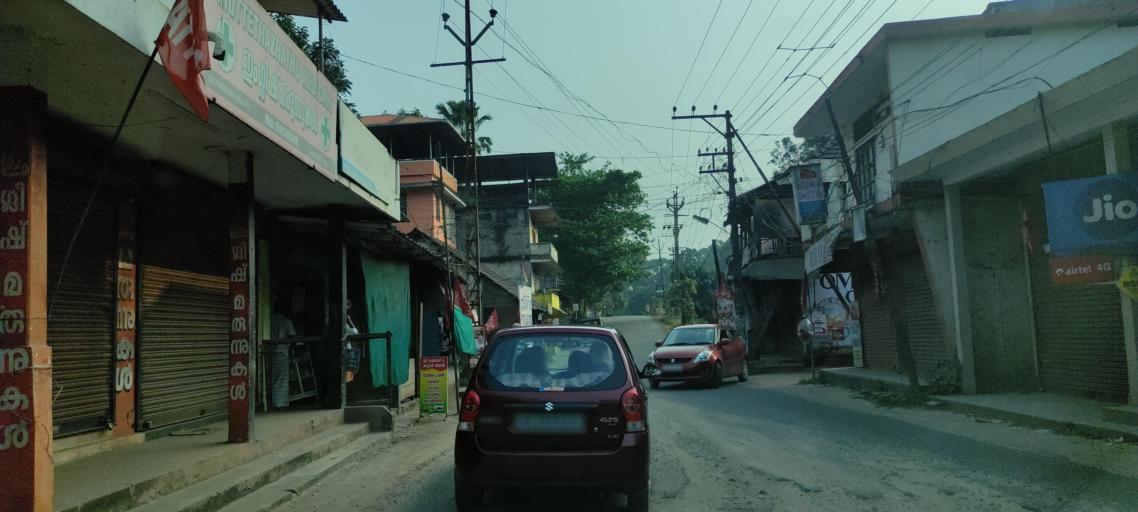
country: IN
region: Kerala
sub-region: Kottayam
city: Vaikam
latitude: 9.7157
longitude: 76.4756
